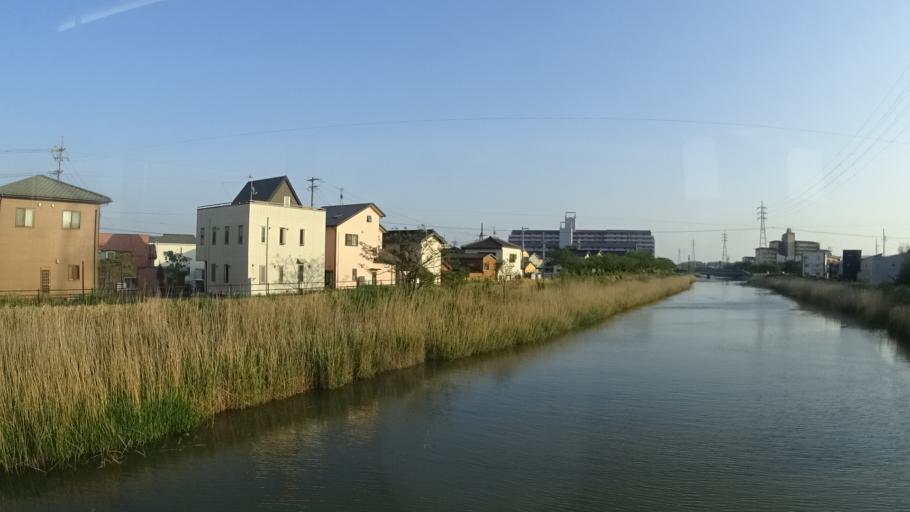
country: JP
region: Aichi
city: Tahara
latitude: 34.6668
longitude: 137.2715
